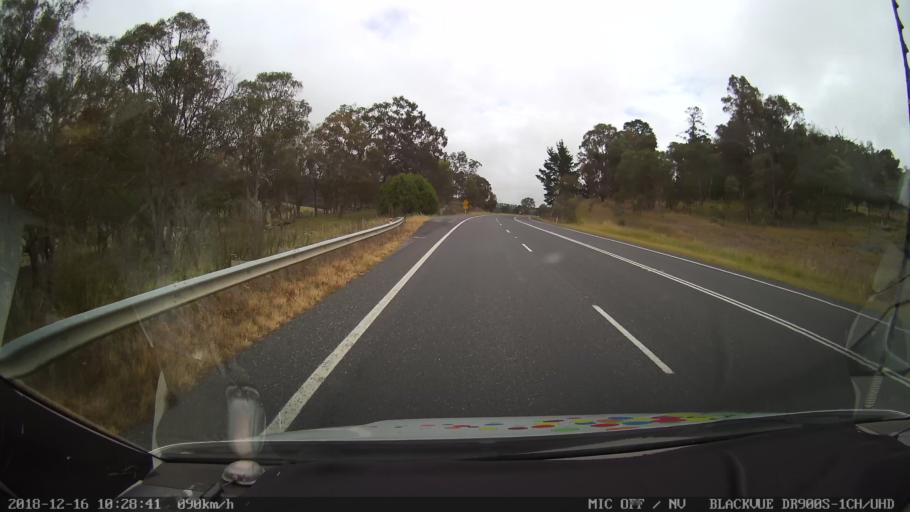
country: AU
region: New South Wales
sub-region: Tenterfield Municipality
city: Carrolls Creek
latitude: -29.1181
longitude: 151.9965
